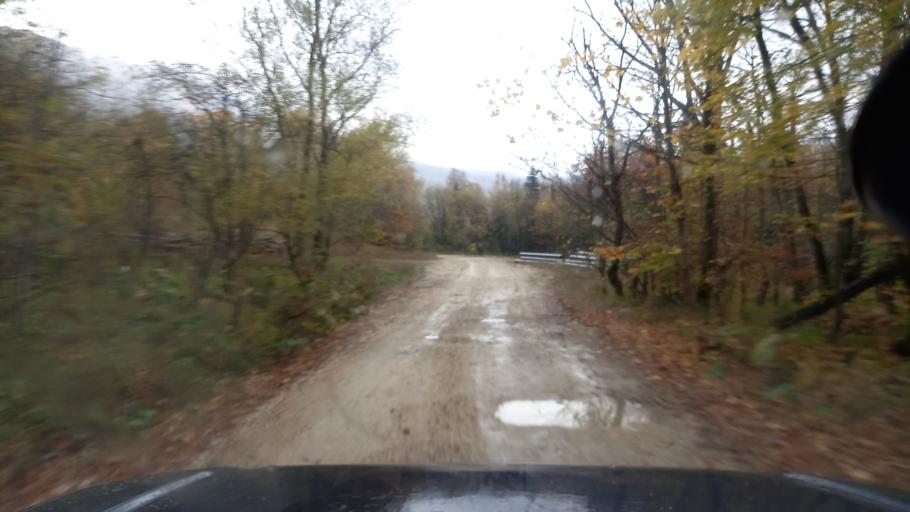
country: RU
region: Krasnodarskiy
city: Neftegorsk
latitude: 44.0397
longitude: 39.8335
